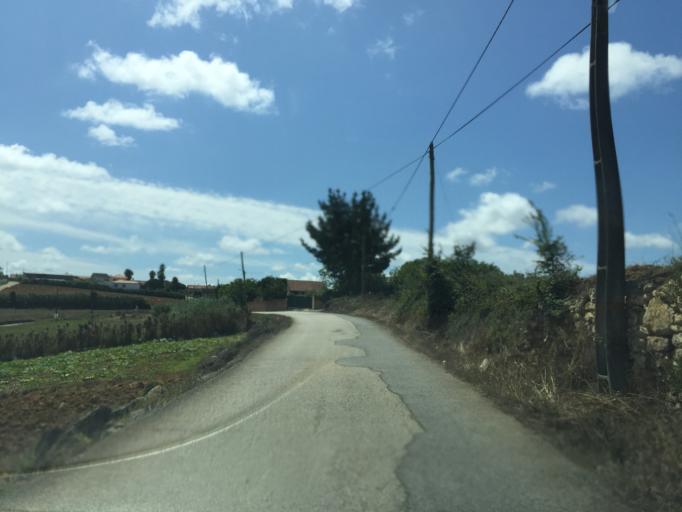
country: PT
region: Leiria
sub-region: Bombarral
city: Bombarral
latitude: 39.2841
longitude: -9.2247
